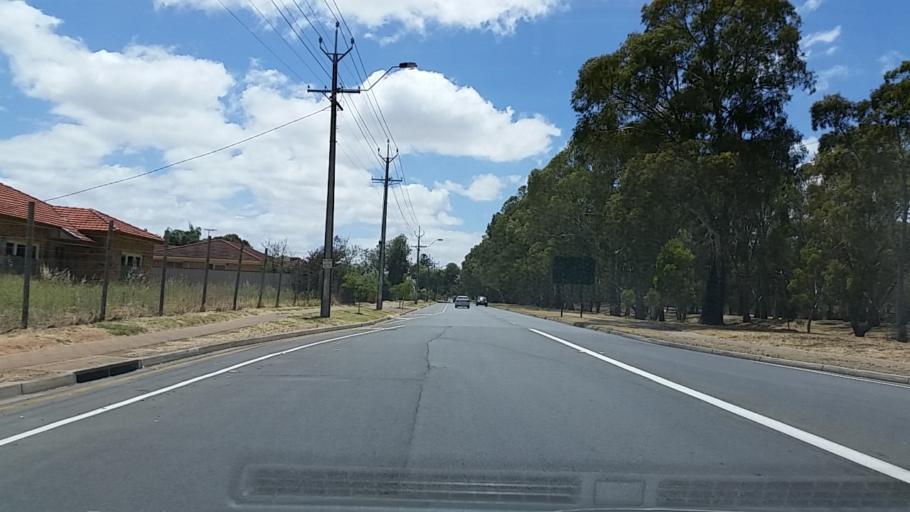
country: AU
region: South Australia
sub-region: Salisbury
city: Salisbury
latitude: -34.7723
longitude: 138.6167
